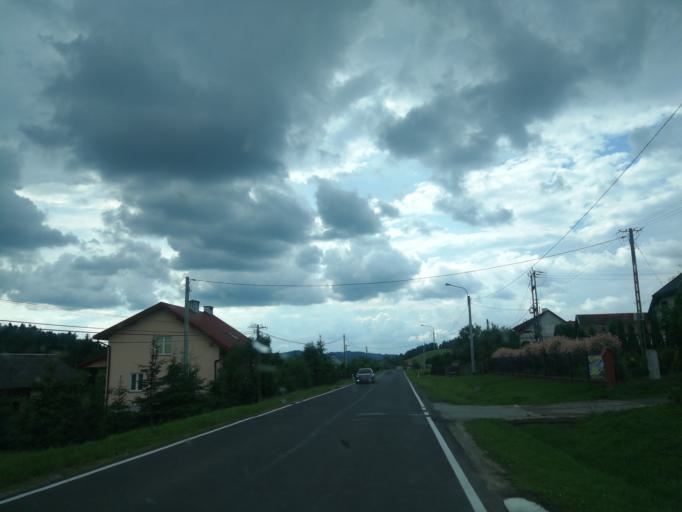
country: PL
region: Subcarpathian Voivodeship
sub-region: Powiat leski
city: Olszanica
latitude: 49.4505
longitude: 22.4343
